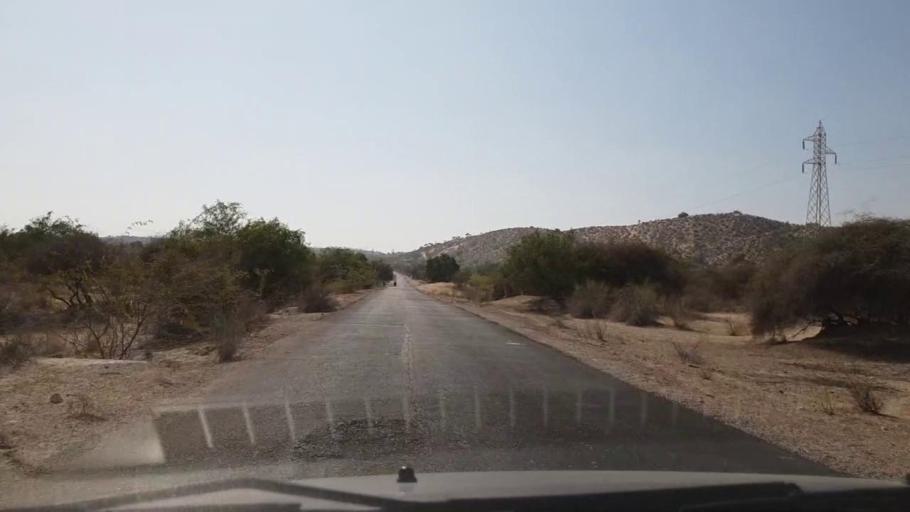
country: PK
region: Sindh
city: Mithi
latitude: 24.6454
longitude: 69.7476
